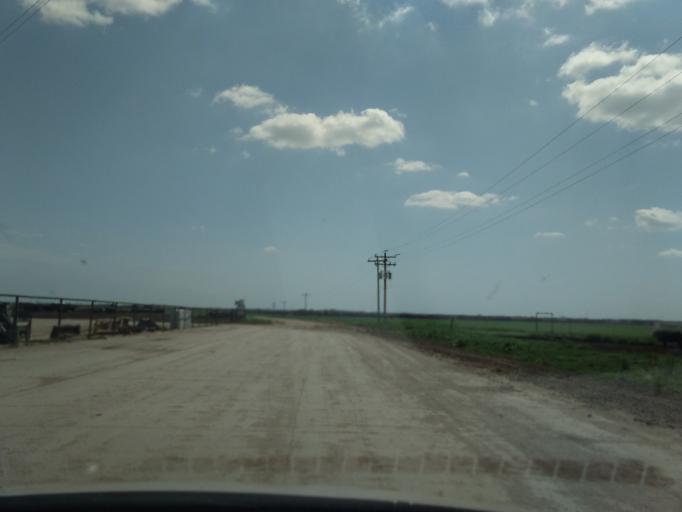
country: US
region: Nebraska
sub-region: Thayer County
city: Hebron
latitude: 40.3292
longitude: -97.4359
